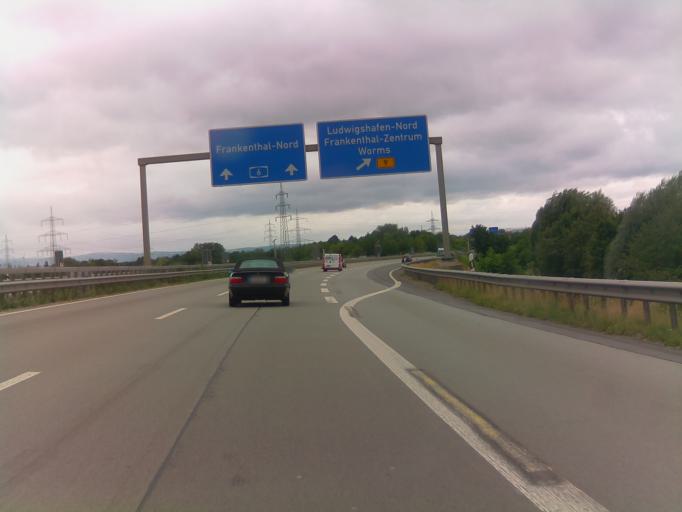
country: DE
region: Rheinland-Pfalz
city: Frankenthal
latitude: 49.5460
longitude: 8.4040
